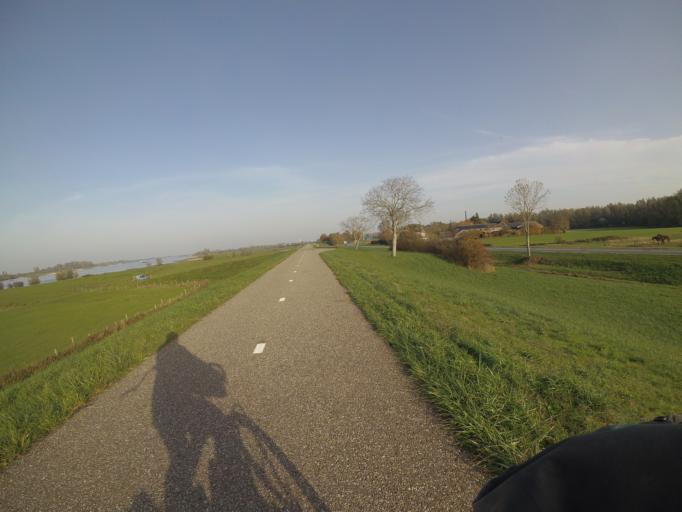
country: NL
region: Gelderland
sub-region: Gemeente Maasdriel
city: Heerewaarden
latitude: 51.8021
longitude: 5.3629
